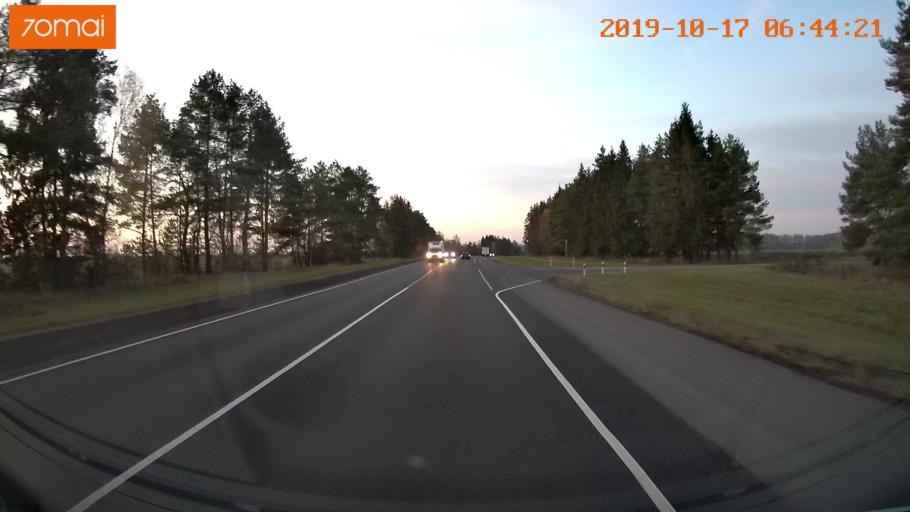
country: RU
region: Vladimir
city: Kideksha
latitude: 56.5739
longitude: 40.5545
